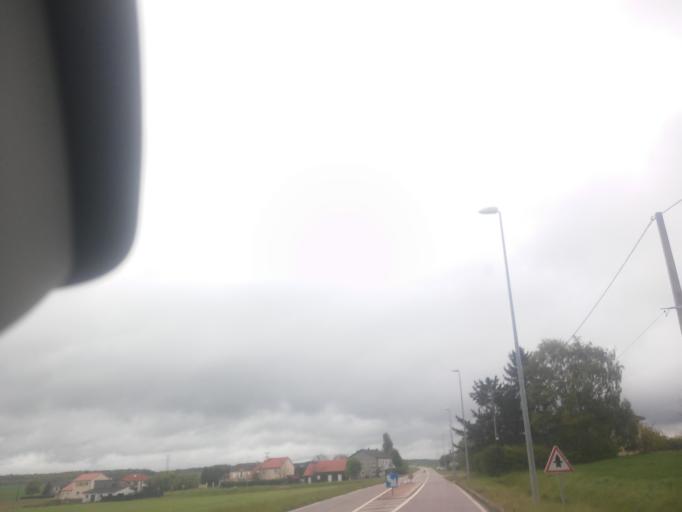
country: FR
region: Lorraine
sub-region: Departement de la Moselle
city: Vigy
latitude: 49.1840
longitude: 6.3306
